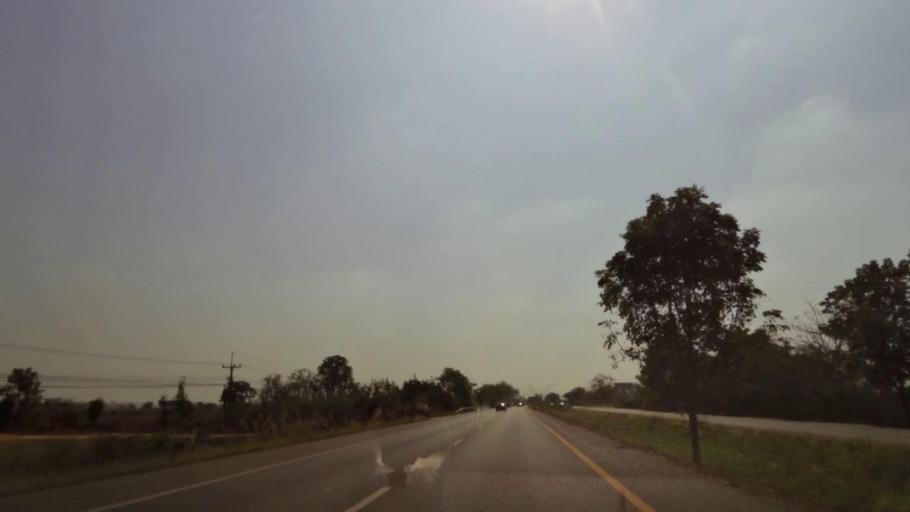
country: TH
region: Phichit
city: Wachira Barami
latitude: 16.4739
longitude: 100.1472
